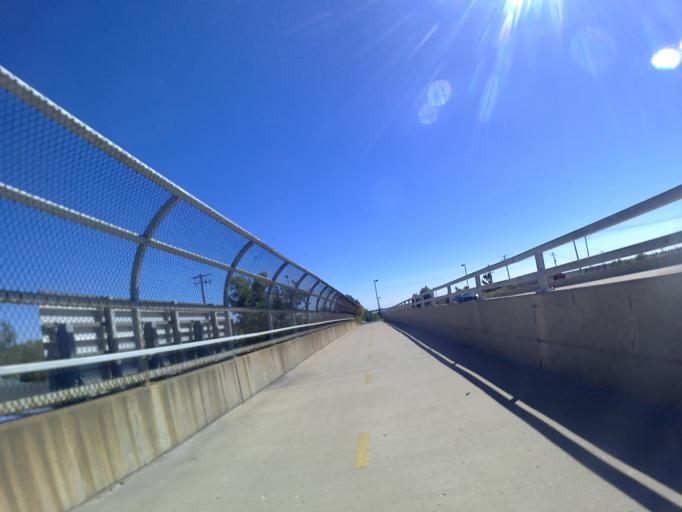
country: US
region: Illinois
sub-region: Cook County
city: Lemont
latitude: 41.7080
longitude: -88.0244
